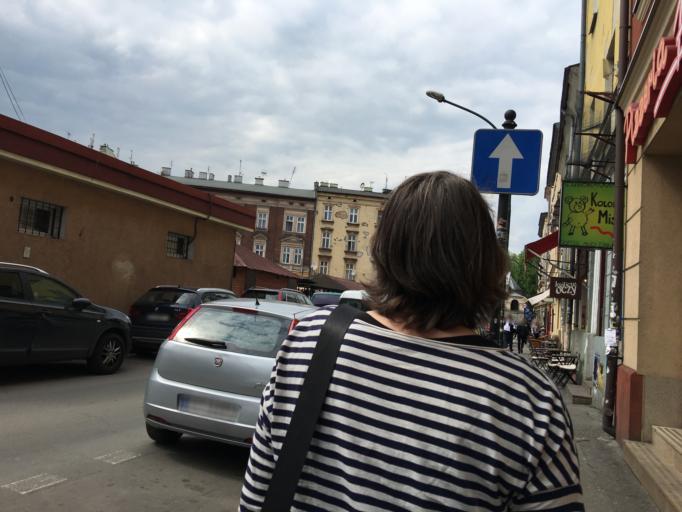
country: PL
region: Lesser Poland Voivodeship
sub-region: Krakow
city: Krakow
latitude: 50.0516
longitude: 19.9456
